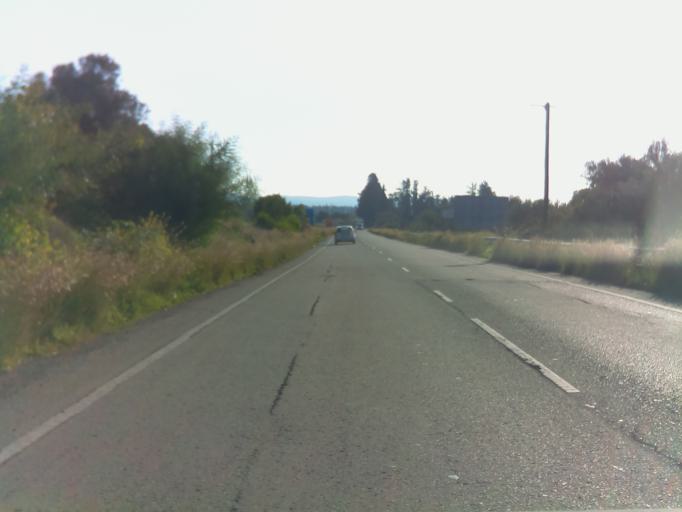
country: CY
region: Pafos
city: Paphos
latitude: 34.7359
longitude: 32.4915
